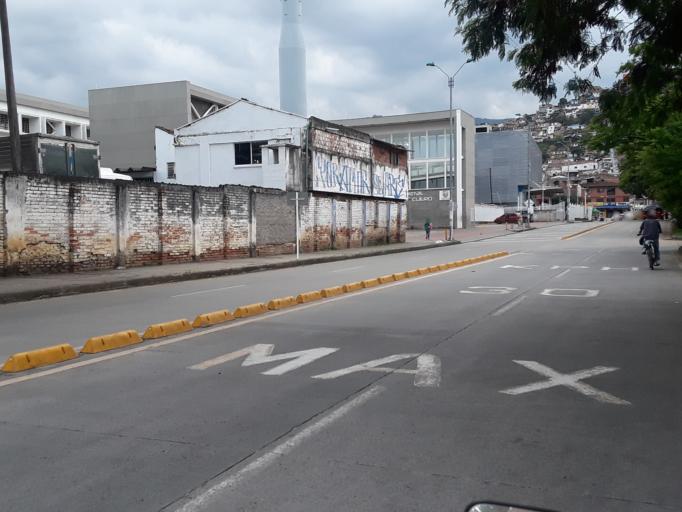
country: CO
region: Valle del Cauca
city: Cali
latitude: 3.4173
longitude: -76.5527
